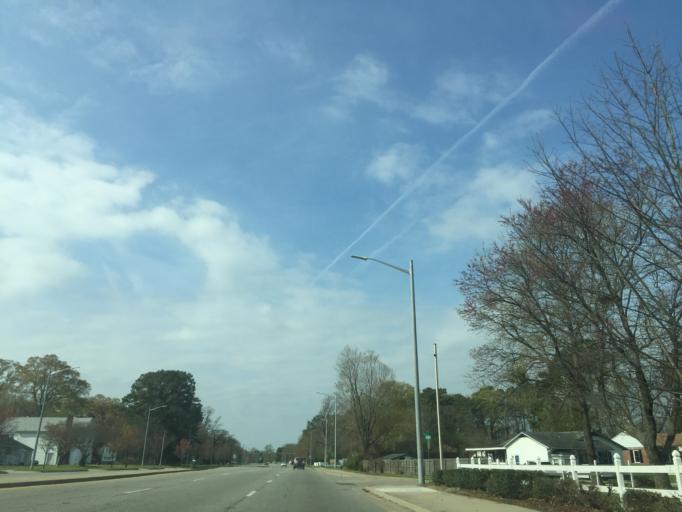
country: US
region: Virginia
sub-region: City of Newport News
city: Newport News
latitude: 37.0632
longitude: -76.4602
